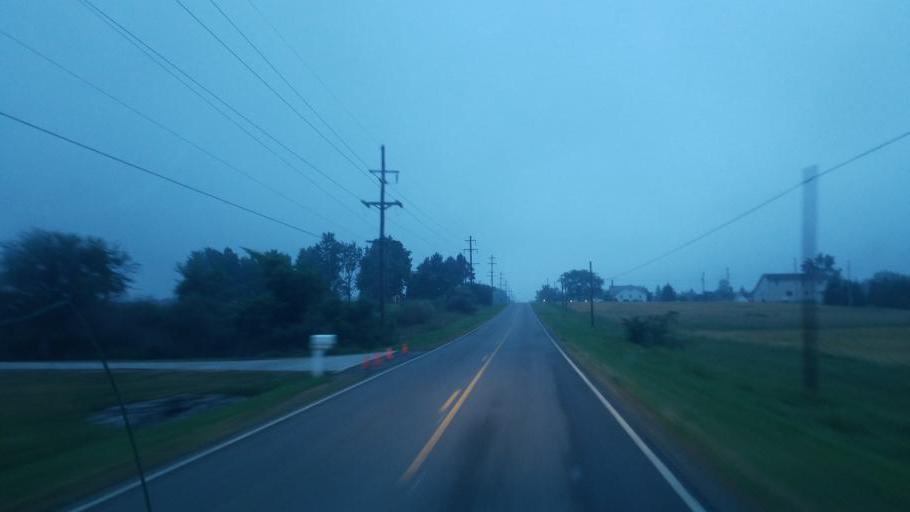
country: US
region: Ohio
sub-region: Defiance County
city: Hicksville
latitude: 41.3270
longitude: -84.7667
